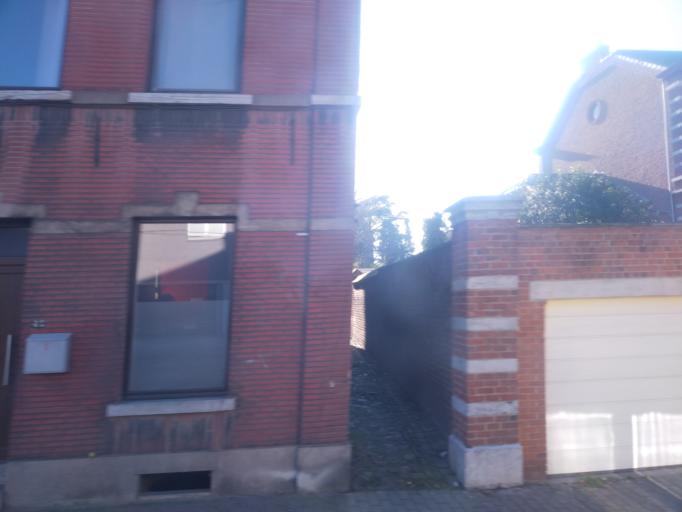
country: BE
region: Wallonia
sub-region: Province du Hainaut
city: Charleroi
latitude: 50.3996
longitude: 4.4493
